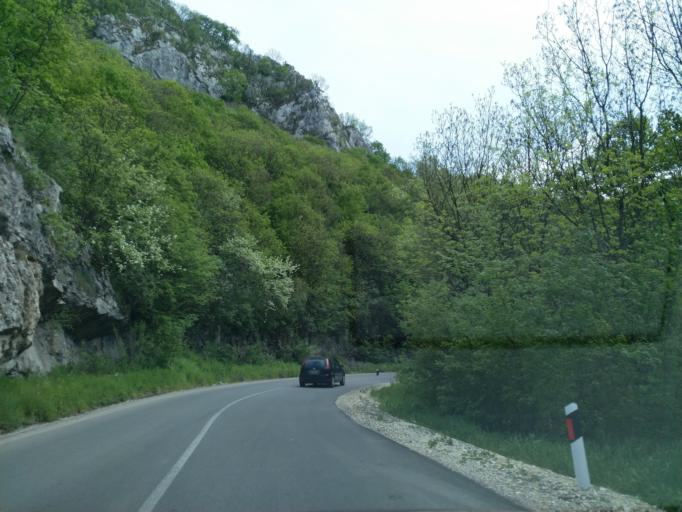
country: RS
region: Central Serbia
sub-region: Pomoravski Okrug
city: Despotovac
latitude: 43.9721
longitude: 21.5246
